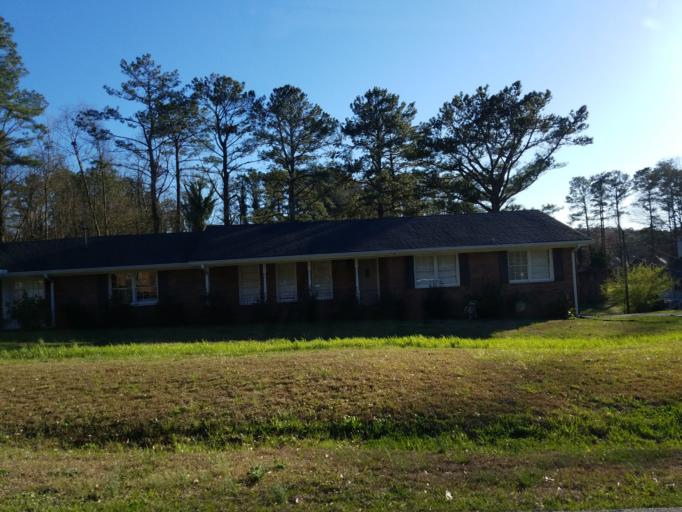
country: US
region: Georgia
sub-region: Cherokee County
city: Woodstock
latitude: 34.0280
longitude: -84.5323
